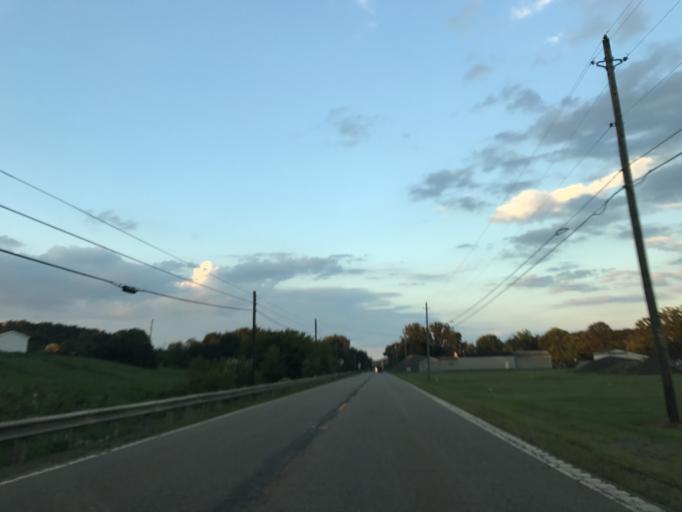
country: US
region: Ohio
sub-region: Stark County
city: Minerva
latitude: 40.7395
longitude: -80.9533
